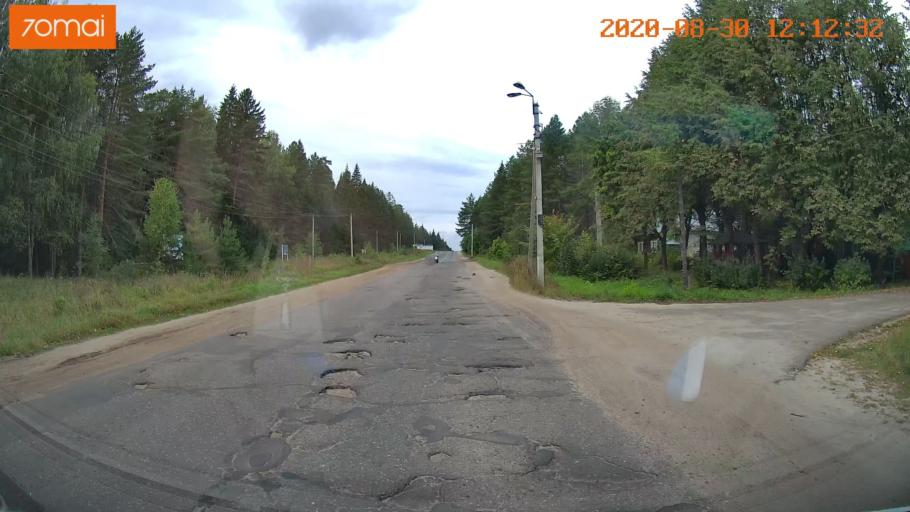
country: RU
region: Ivanovo
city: Yur'yevets
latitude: 57.3116
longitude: 43.0906
